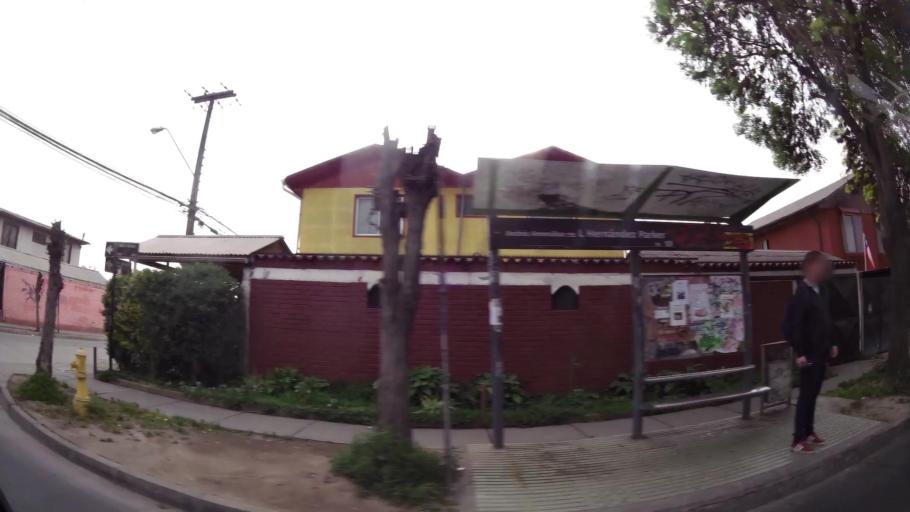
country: CL
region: Santiago Metropolitan
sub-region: Provincia de Maipo
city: San Bernardo
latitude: -33.5296
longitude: -70.7685
